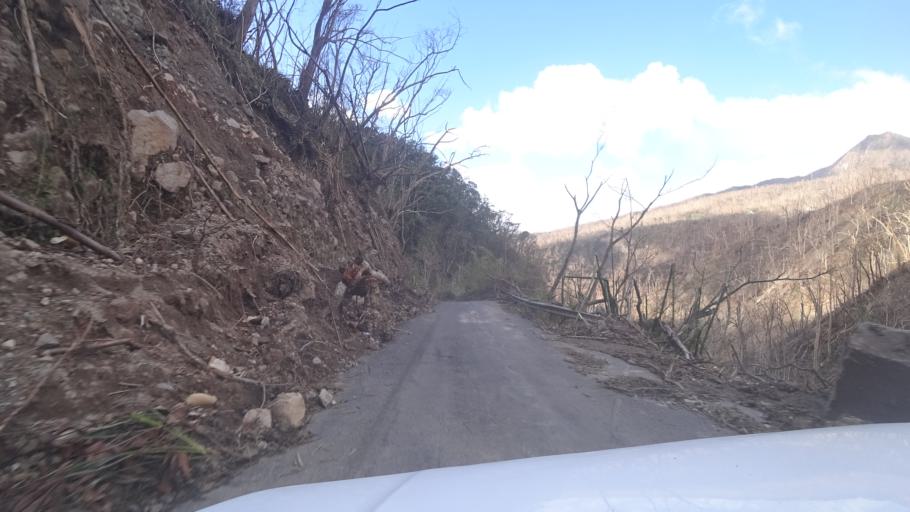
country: DM
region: Saint Luke
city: Pointe Michel
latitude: 15.2664
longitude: -61.3504
